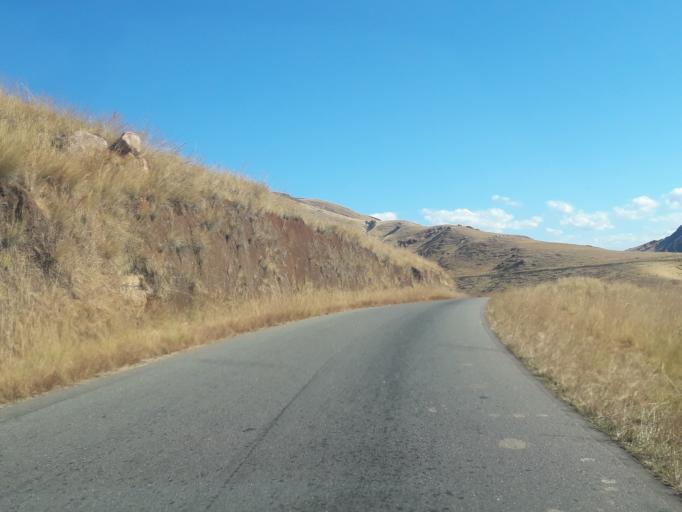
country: MG
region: Analamanga
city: Ankazobe
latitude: -17.6382
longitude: 46.9586
